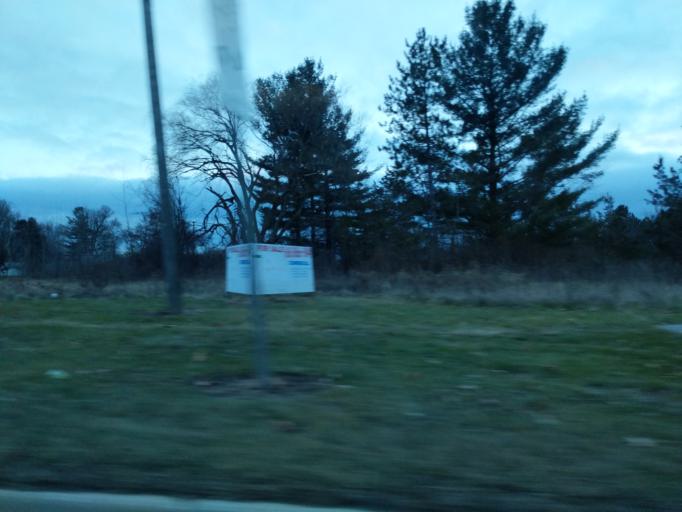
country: US
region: Michigan
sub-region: Lapeer County
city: Almont
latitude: 42.9272
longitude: -83.0482
